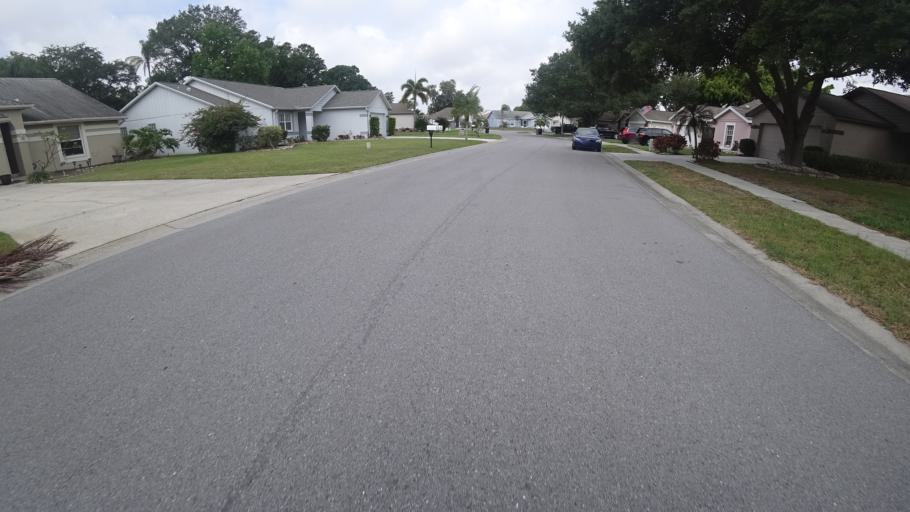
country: US
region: Florida
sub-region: Sarasota County
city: North Sarasota
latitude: 27.4023
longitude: -82.5206
